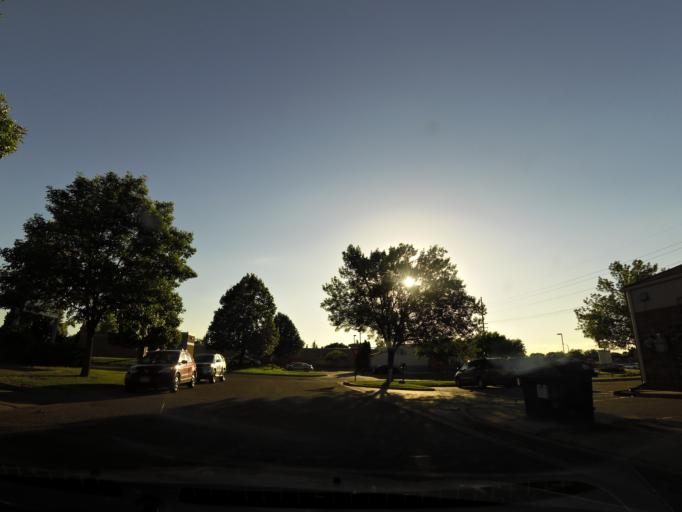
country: US
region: Minnesota
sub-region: Scott County
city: Savage
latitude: 44.7457
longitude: -93.3302
